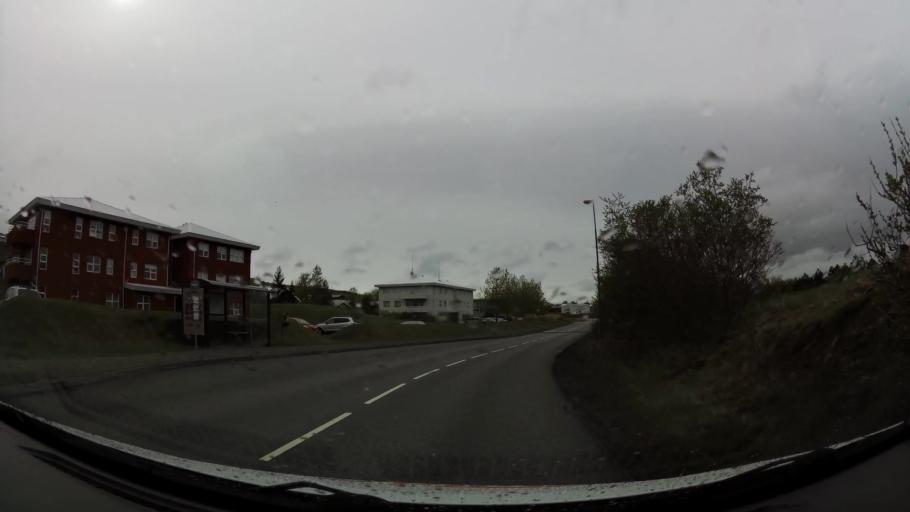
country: IS
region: Capital Region
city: Hafnarfjoerdur
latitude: 64.0589
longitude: -21.9272
